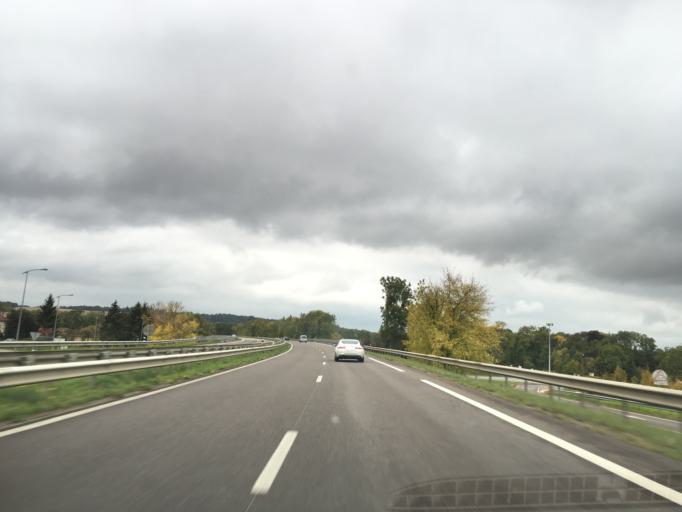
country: FR
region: Lorraine
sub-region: Departement de la Meuse
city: Vacon
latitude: 48.6909
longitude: 5.6245
